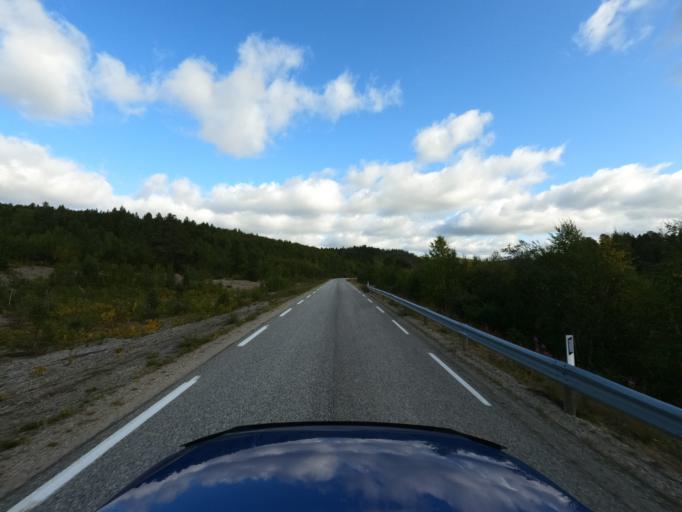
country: NO
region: Finnmark Fylke
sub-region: Porsanger
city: Lakselv
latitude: 69.4240
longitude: 24.8564
